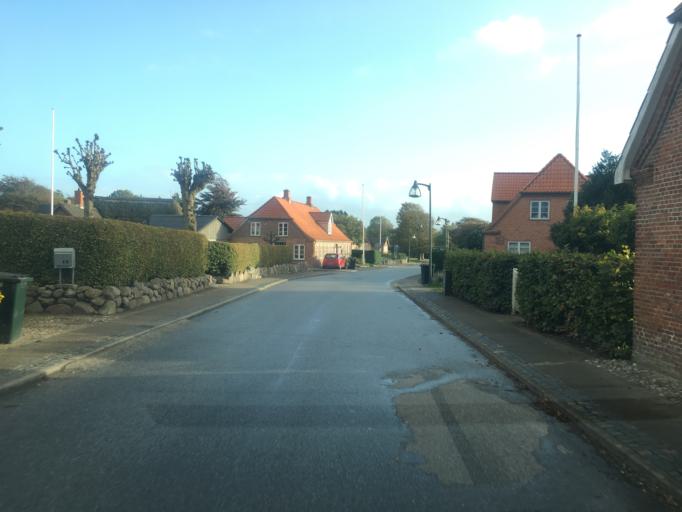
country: DE
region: Schleswig-Holstein
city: Aventoft
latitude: 54.9401
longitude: 8.8032
